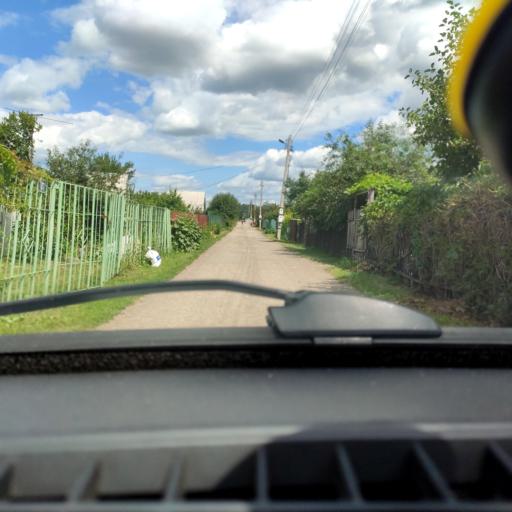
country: RU
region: Samara
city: Podstepki
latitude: 53.6009
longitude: 49.2252
